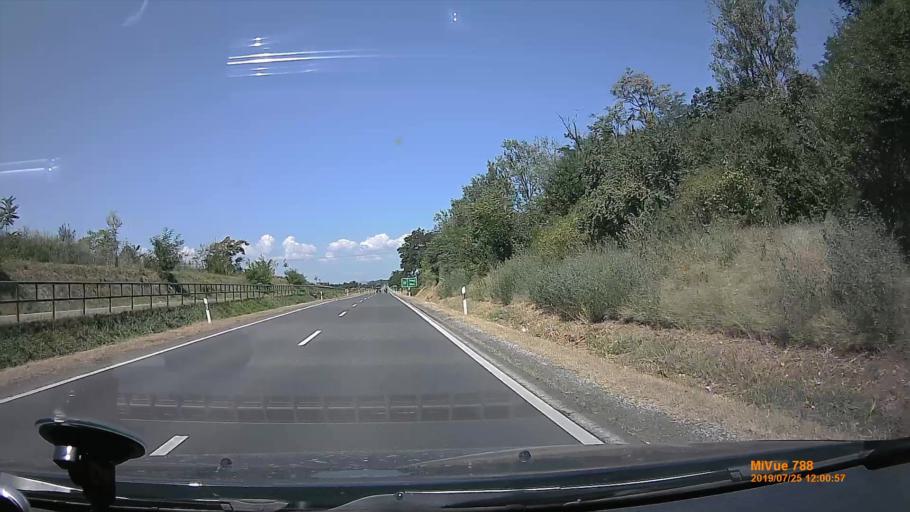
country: HU
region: Szabolcs-Szatmar-Bereg
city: Nyirtelek
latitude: 48.0394
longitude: 21.5858
